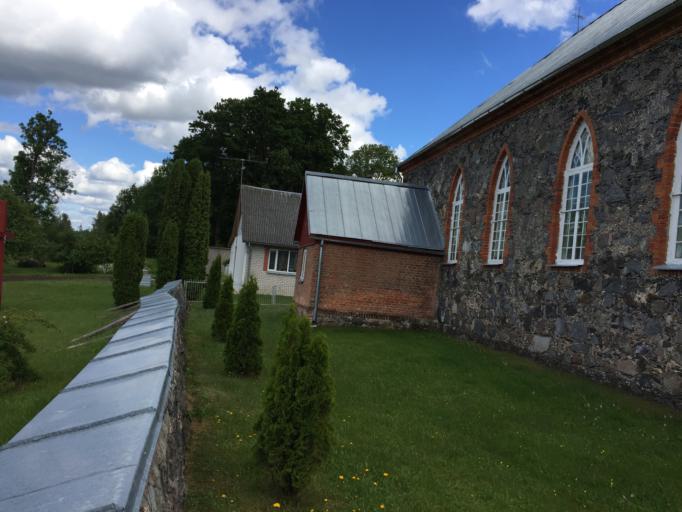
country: LV
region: Vecumnieki
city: Vecumnieki
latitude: 56.4256
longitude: 24.5126
